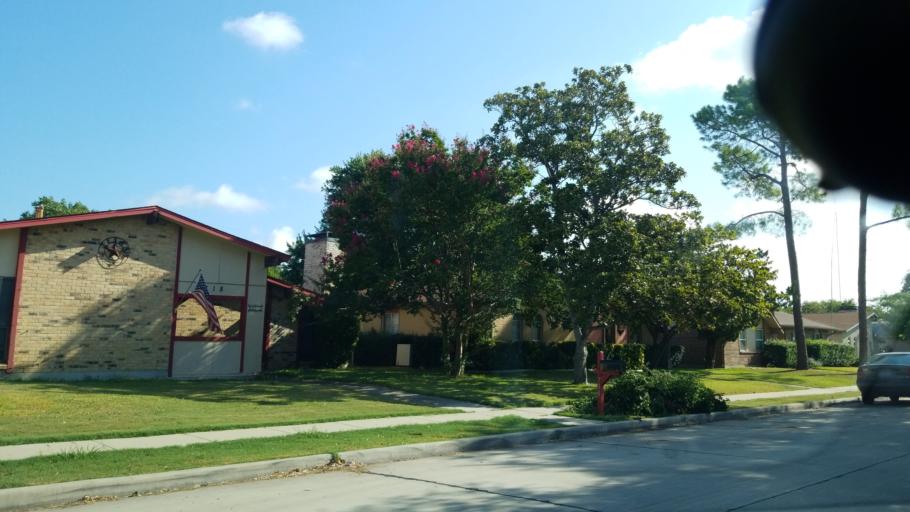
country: US
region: Texas
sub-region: Dallas County
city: Grand Prairie
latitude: 32.6961
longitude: -96.9957
